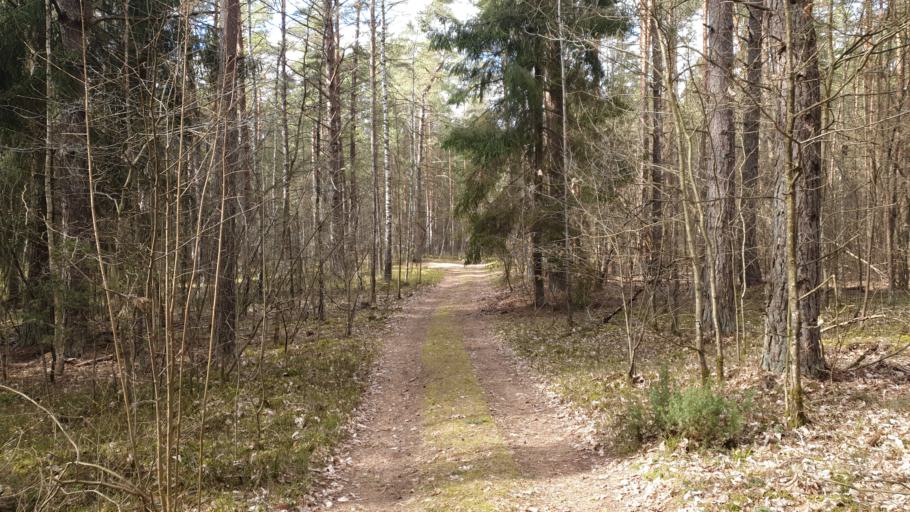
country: LT
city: Grigiskes
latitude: 54.7287
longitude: 25.0317
